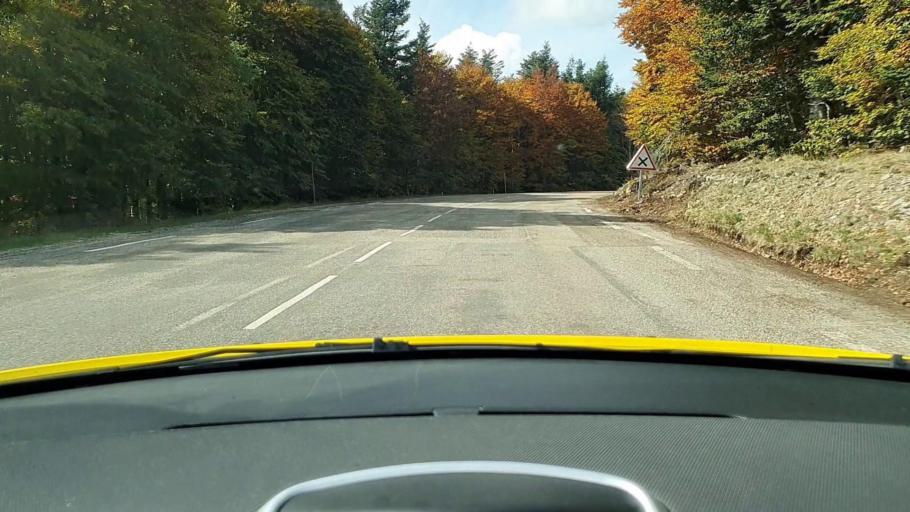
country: FR
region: Languedoc-Roussillon
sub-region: Departement du Gard
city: Valleraugue
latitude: 44.1170
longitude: 3.5566
